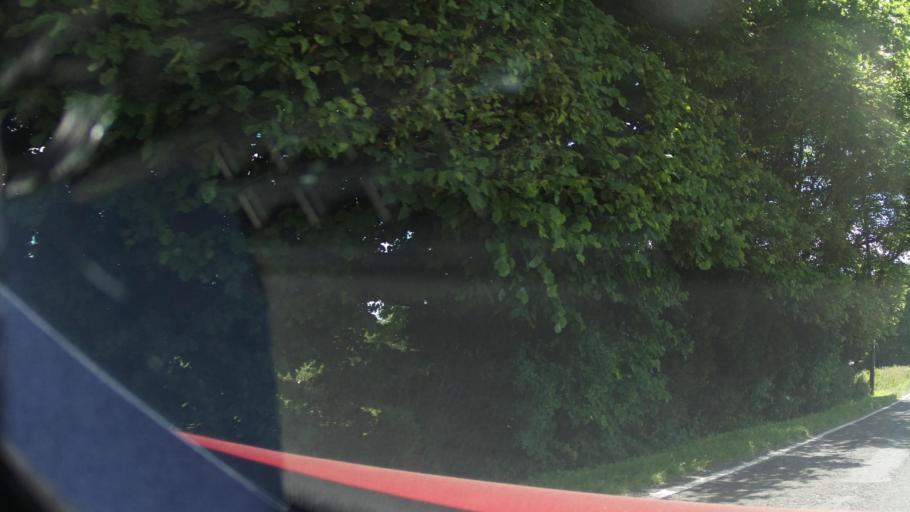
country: GB
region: England
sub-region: Derbyshire
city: Ashbourne
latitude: 53.0805
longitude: -1.7597
